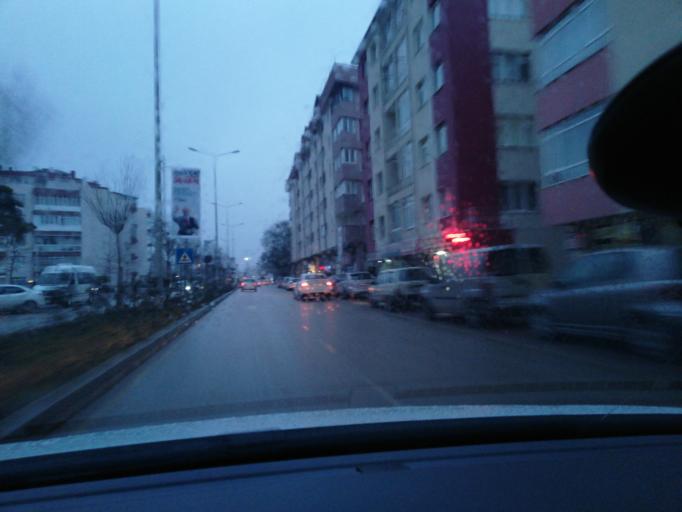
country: TR
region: Bolu
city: Bolu
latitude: 40.7309
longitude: 31.5960
